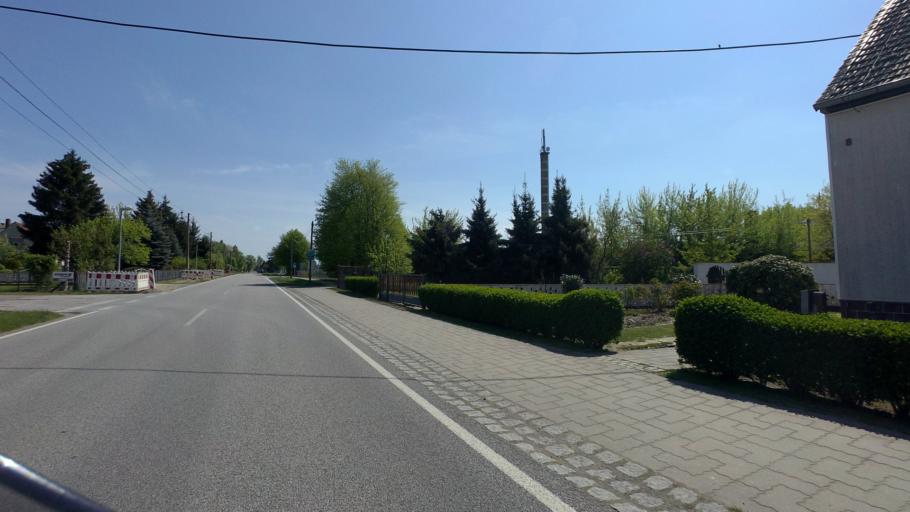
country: DE
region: Brandenburg
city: Schlepzig
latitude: 52.0465
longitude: 14.0183
